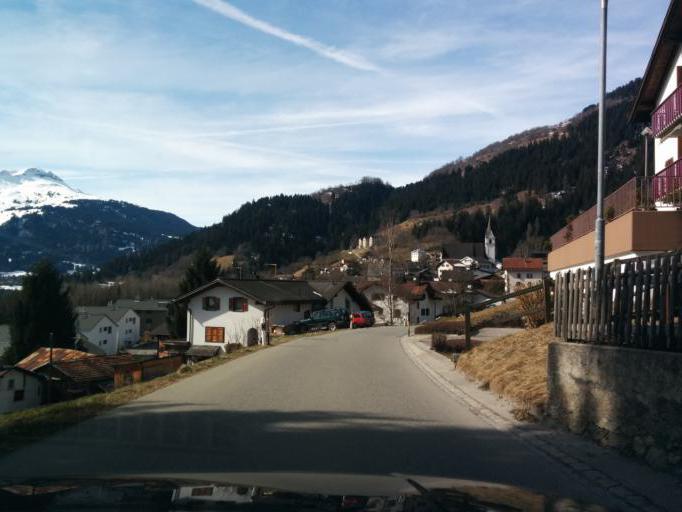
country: CH
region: Grisons
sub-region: Surselva District
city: Laax
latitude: 46.7891
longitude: 9.2327
